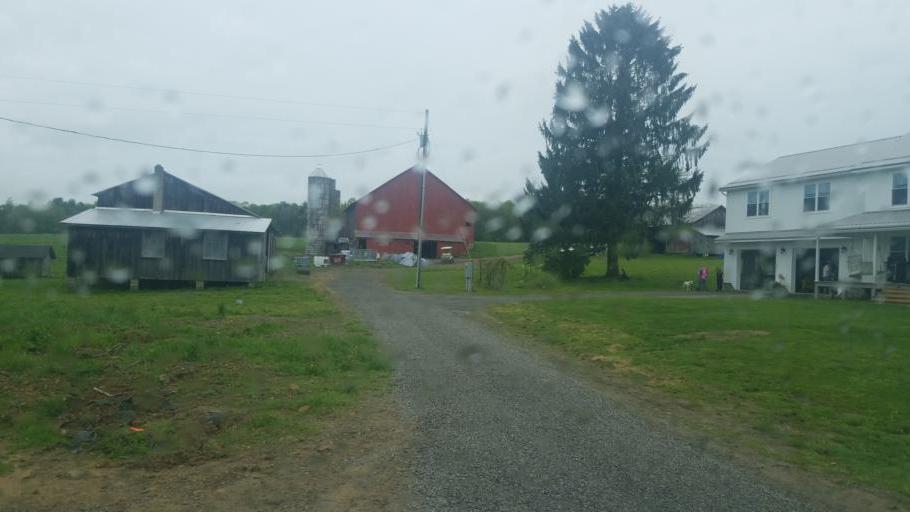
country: US
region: Pennsylvania
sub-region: Forest County
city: Tionesta
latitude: 41.3970
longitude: -79.3931
